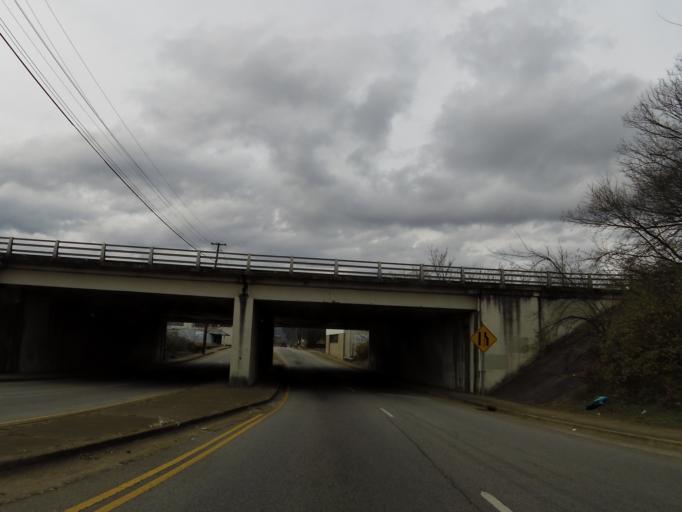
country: US
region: Tennessee
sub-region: Hamilton County
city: Chattanooga
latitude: 35.0324
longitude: -85.2974
